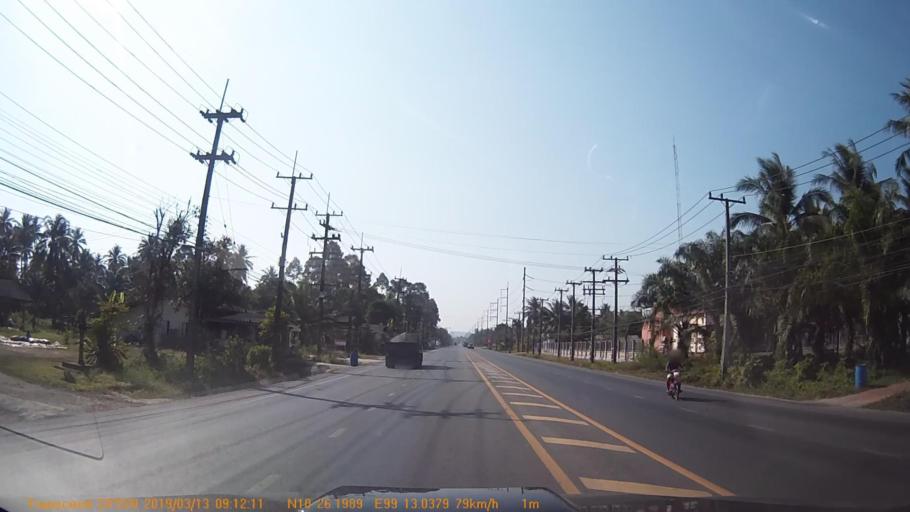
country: TH
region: Chumphon
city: Chumphon
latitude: 10.4364
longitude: 99.2174
